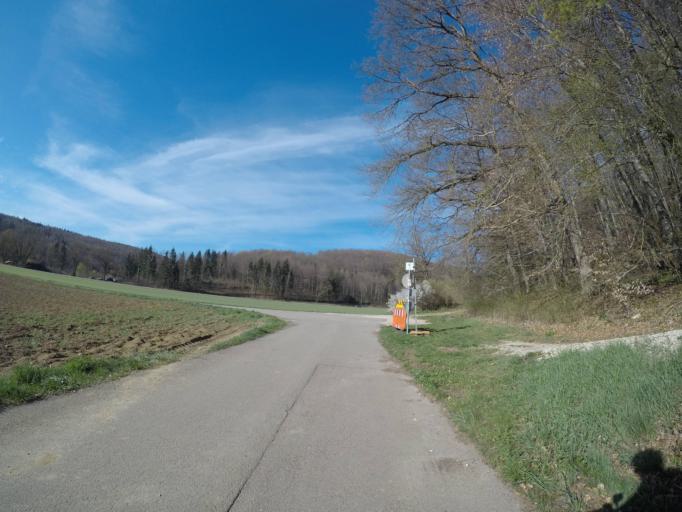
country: DE
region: Baden-Wuerttemberg
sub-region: Tuebingen Region
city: Allmendingen
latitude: 48.3484
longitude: 9.7086
